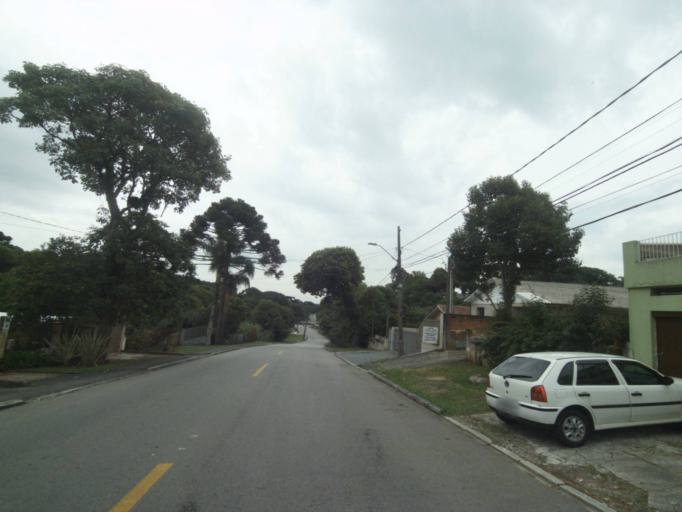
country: BR
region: Parana
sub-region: Curitiba
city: Curitiba
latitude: -25.4134
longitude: -49.2992
